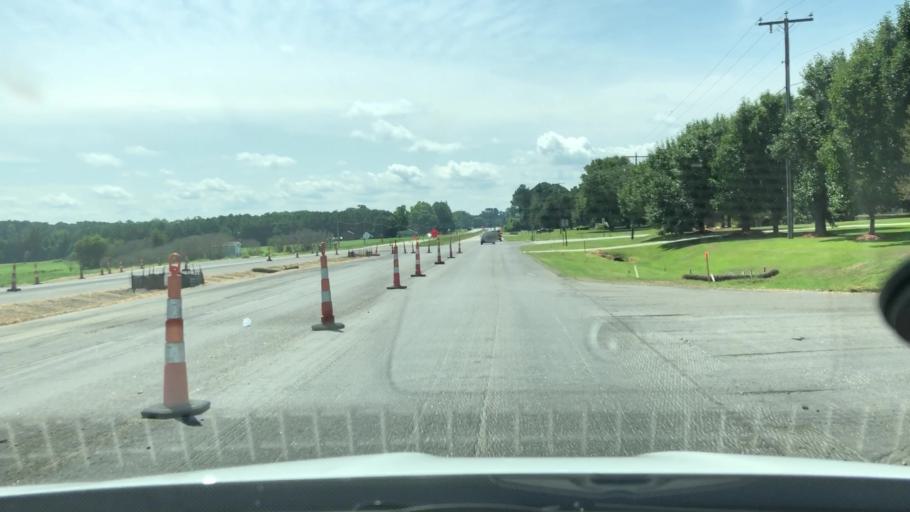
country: US
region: North Carolina
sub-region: Martin County
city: Williamston
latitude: 35.8122
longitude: -77.0639
